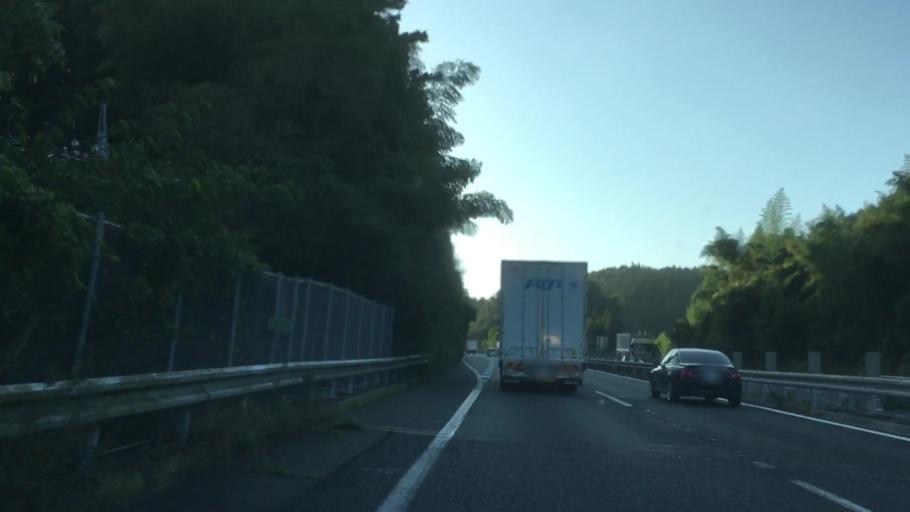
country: JP
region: Yamaguchi
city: Onoda
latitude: 34.1169
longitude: 131.1197
